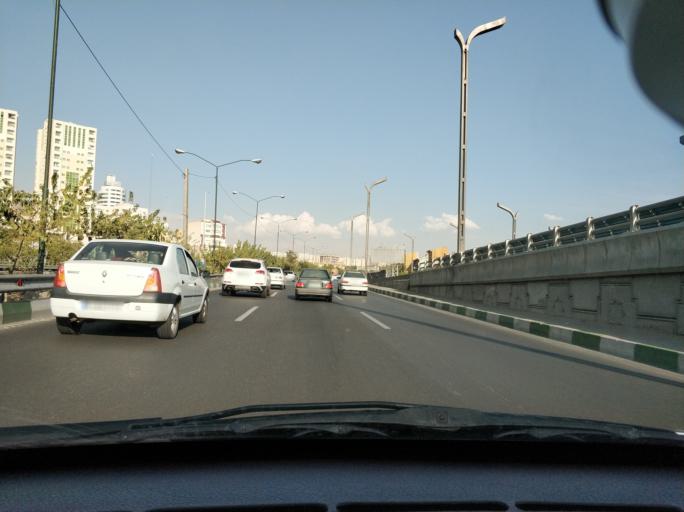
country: IR
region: Tehran
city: Tajrish
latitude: 35.7859
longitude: 51.4959
